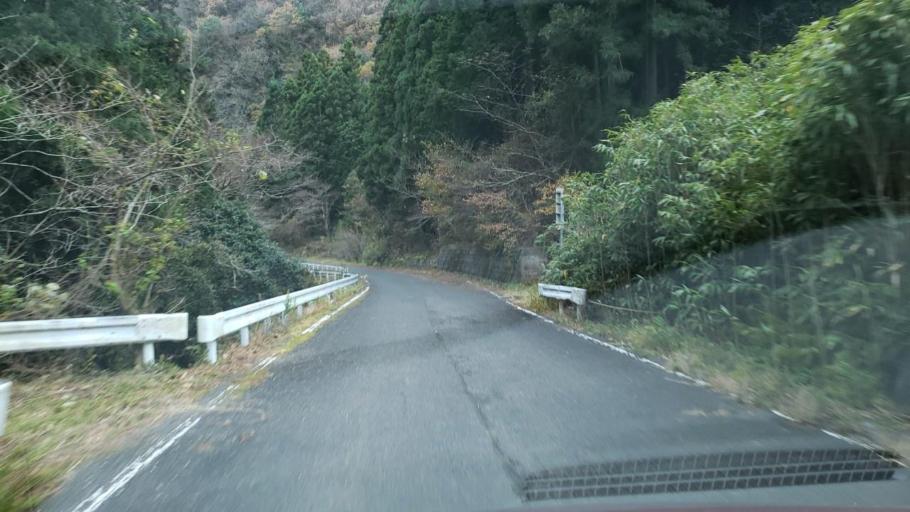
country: JP
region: Tokushima
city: Wakimachi
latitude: 34.1443
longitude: 134.2289
